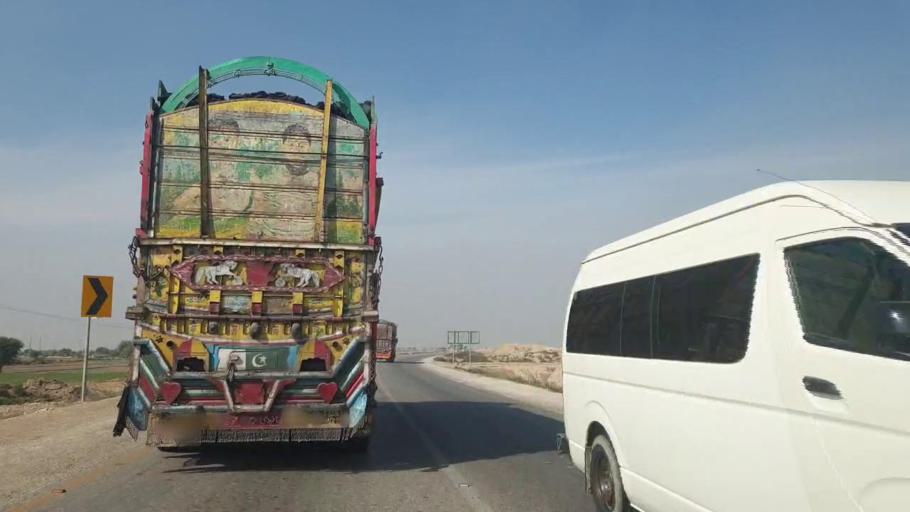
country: PK
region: Sindh
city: Sann
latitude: 25.9544
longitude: 68.1949
